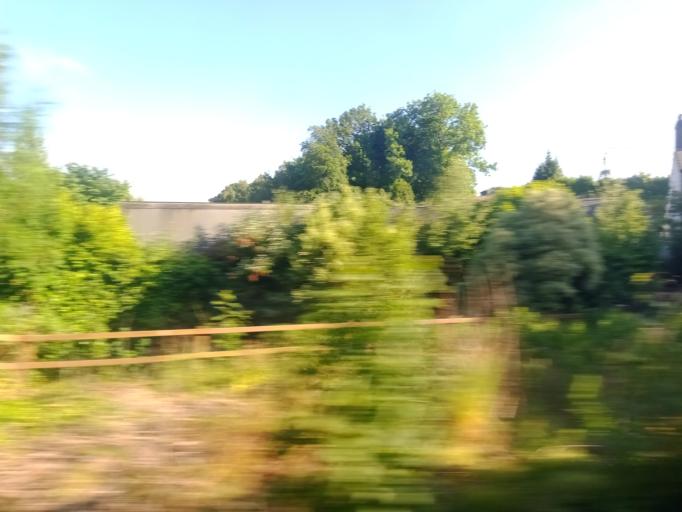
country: GB
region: Wales
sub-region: Gwynedd
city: Bangor
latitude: 53.2147
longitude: -4.0980
